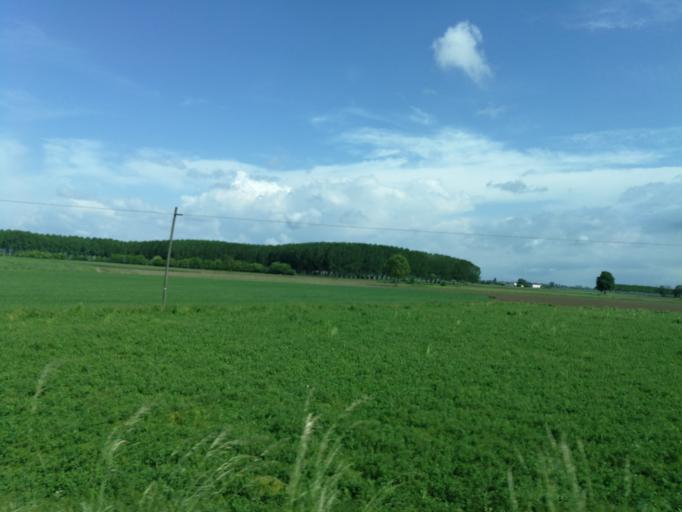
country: IT
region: Piedmont
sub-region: Provincia di Cuneo
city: Moretta
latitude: 44.7737
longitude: 7.5472
